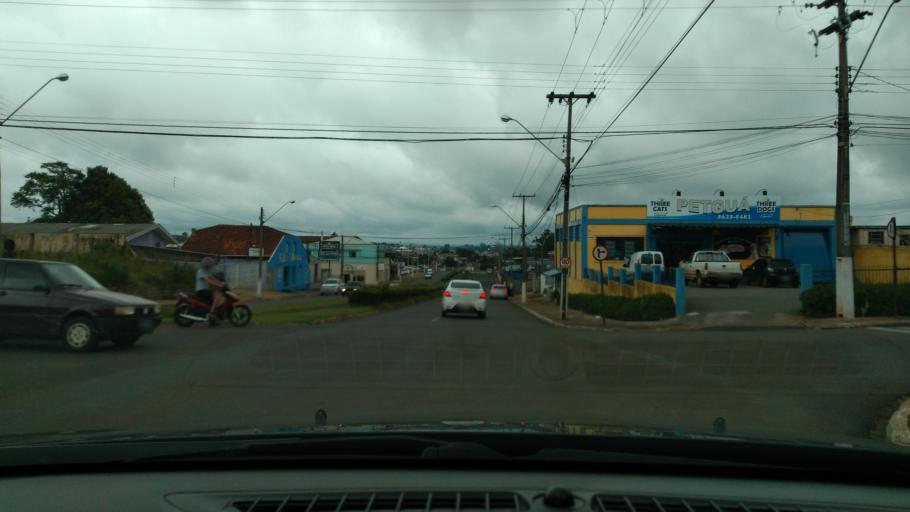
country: BR
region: Parana
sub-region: Guarapuava
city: Guarapuava
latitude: -25.3913
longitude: -51.4788
